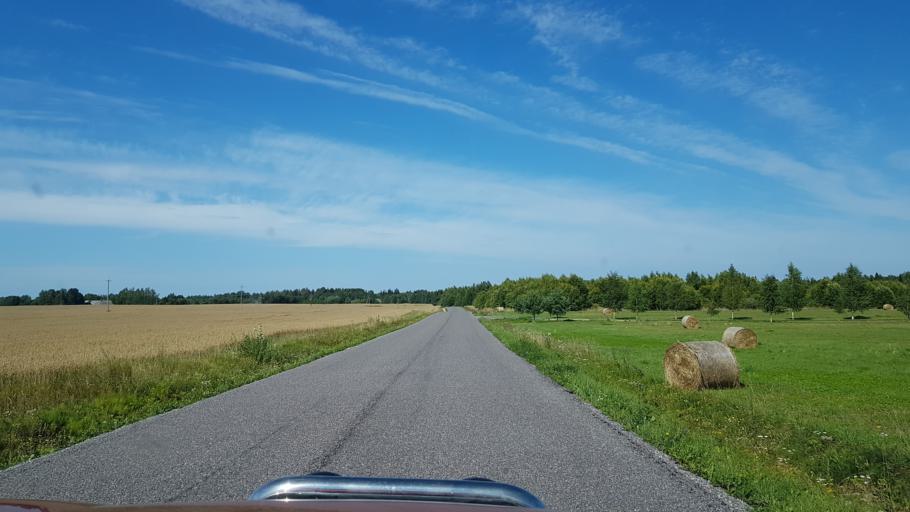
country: EE
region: Tartu
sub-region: Elva linn
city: Elva
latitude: 58.2479
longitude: 26.3449
